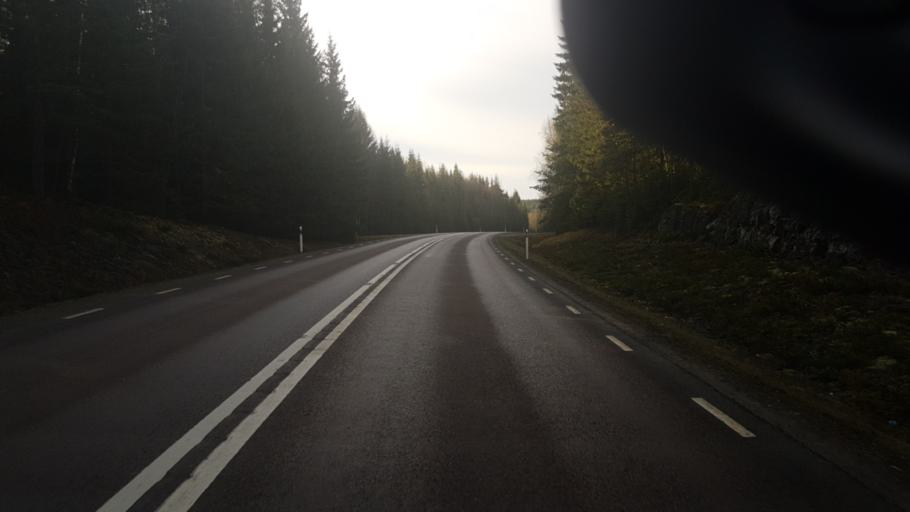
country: SE
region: Vaermland
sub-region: Arvika Kommun
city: Arvika
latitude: 59.7213
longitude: 12.5227
